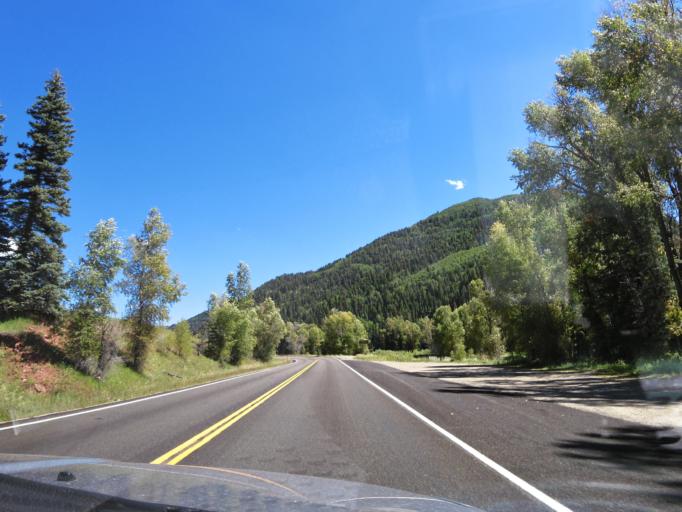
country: US
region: Colorado
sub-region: Montezuma County
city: Mancos
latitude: 37.6005
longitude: -108.1141
